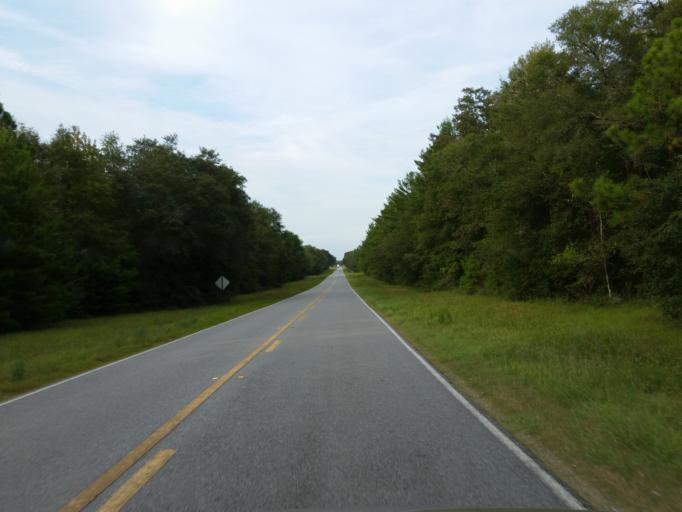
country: US
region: Florida
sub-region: Madison County
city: Madison
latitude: 30.5131
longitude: -83.2187
